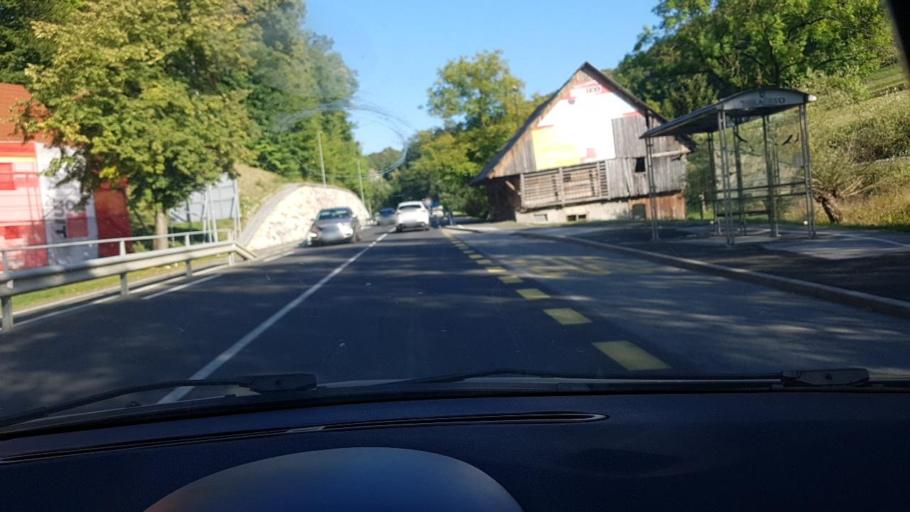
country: SI
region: Rogaska Slatina
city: Rogaska Slatina
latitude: 46.2395
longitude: 15.6055
